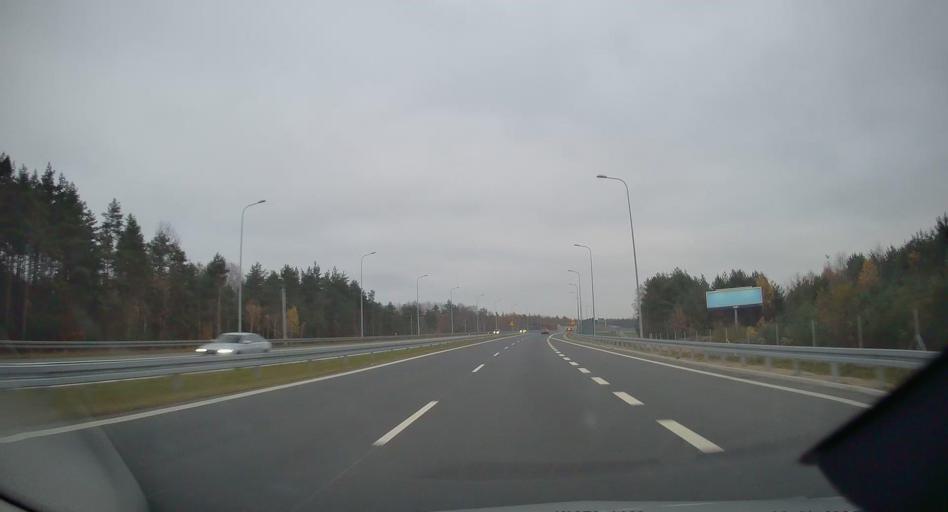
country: PL
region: Silesian Voivodeship
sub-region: Powiat bedzinski
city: Mierzecice
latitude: 50.4562
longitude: 19.0901
